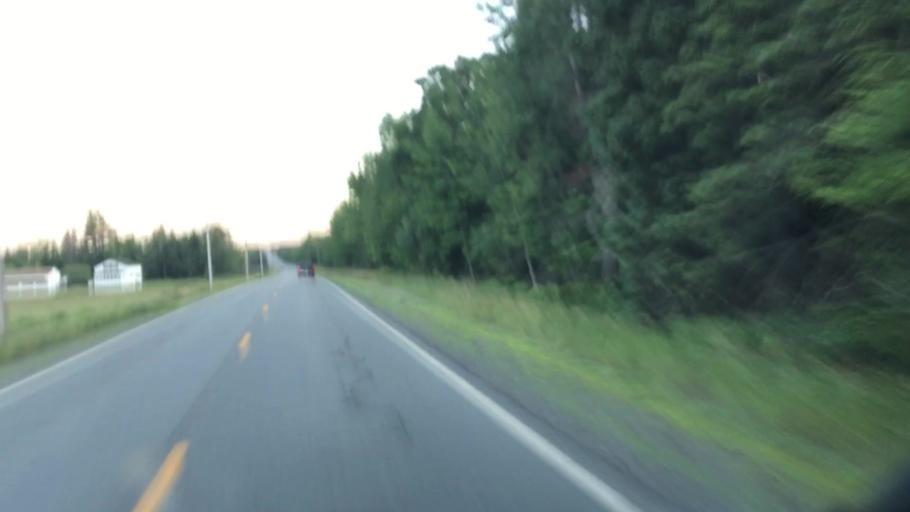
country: US
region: Maine
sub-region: Penobscot County
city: Medway
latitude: 45.6125
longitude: -68.3047
